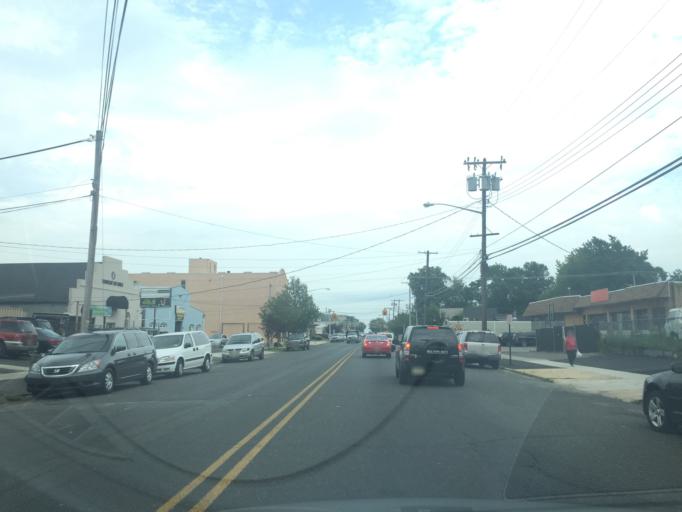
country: US
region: New Jersey
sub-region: Monmouth County
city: Asbury Park
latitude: 40.2212
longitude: -74.0159
